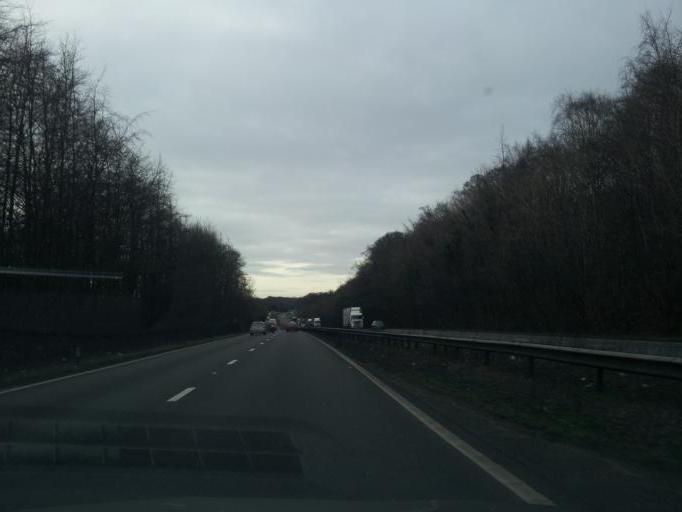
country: GB
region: England
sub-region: Lincolnshire
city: Grantham
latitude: 52.8443
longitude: -0.6284
